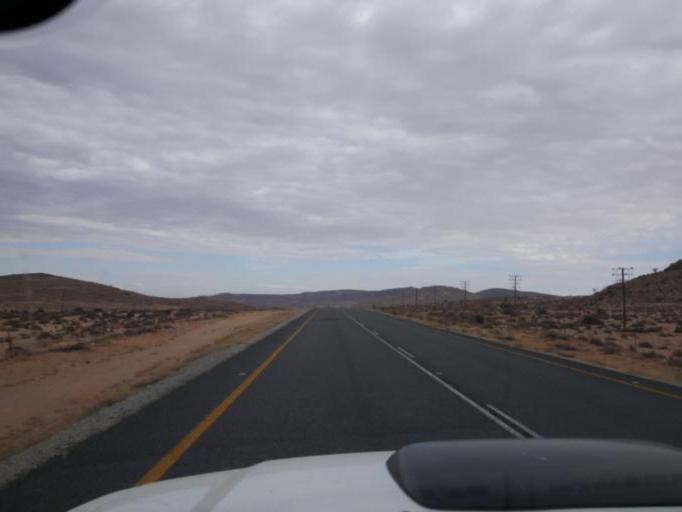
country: ZA
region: Northern Cape
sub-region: Namakwa District Municipality
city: Springbok
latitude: -29.4983
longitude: 17.8434
